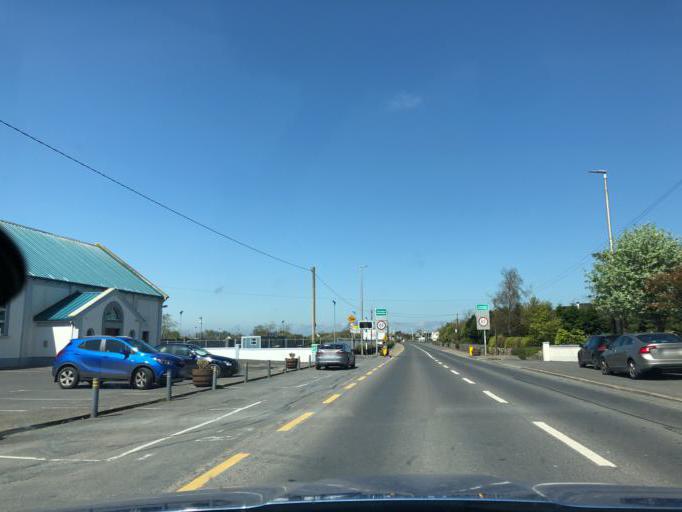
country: IE
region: Connaught
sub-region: County Galway
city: Athenry
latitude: 53.2327
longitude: -8.7392
